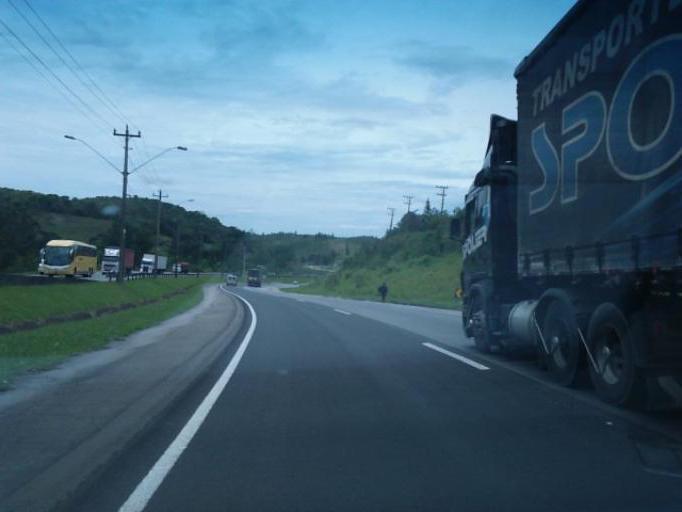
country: BR
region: Sao Paulo
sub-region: Sao Lourenco Da Serra
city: Sao Lourenco da Serra
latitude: -23.8338
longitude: -46.9298
